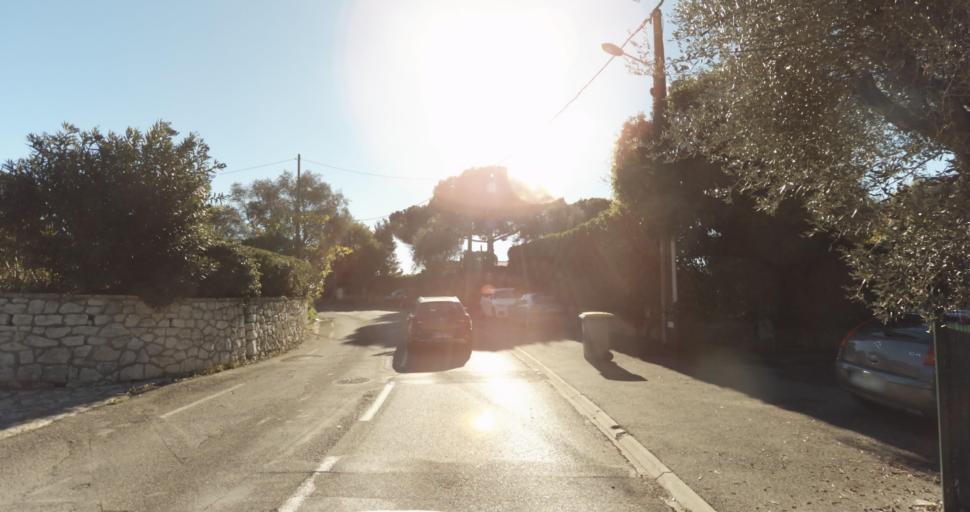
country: FR
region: Provence-Alpes-Cote d'Azur
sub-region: Departement des Alpes-Maritimes
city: Vence
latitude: 43.7262
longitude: 7.0967
